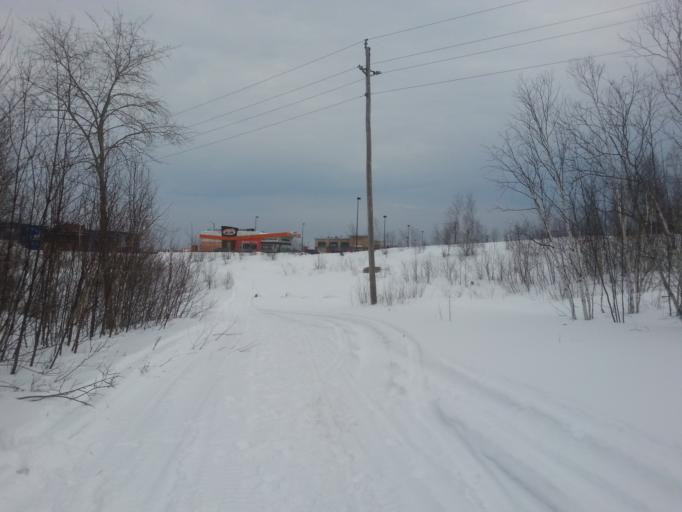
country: CA
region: Ontario
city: Greater Sudbury
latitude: 46.5001
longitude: -80.9505
